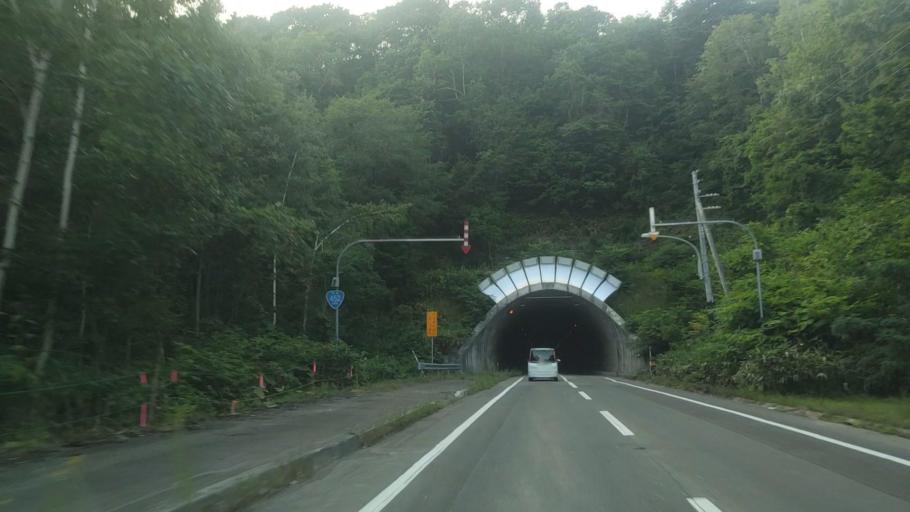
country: JP
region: Hokkaido
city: Bibai
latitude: 43.2384
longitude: 142.0295
